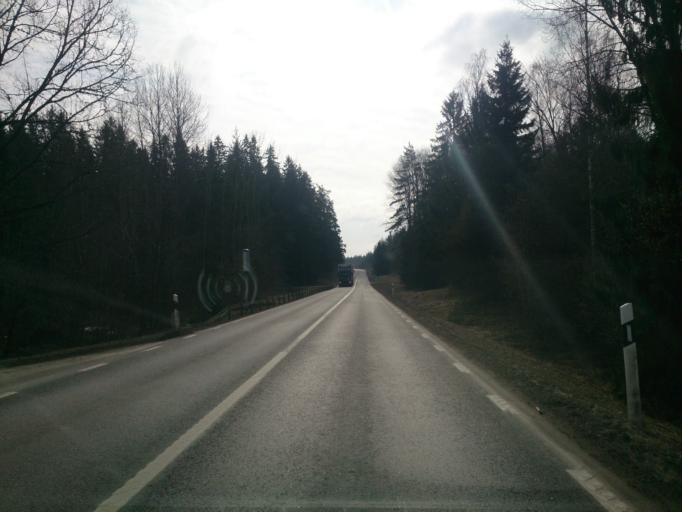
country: SE
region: OEstergoetland
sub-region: Atvidabergs Kommun
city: Atvidaberg
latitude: 58.2480
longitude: 15.9316
